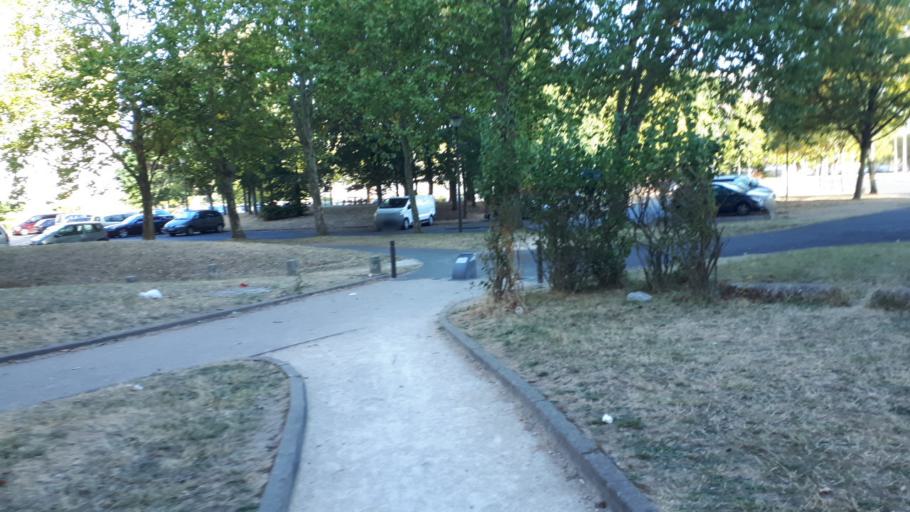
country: FR
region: Centre
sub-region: Departement du Loir-et-Cher
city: Blois
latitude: 47.5907
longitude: 1.3035
